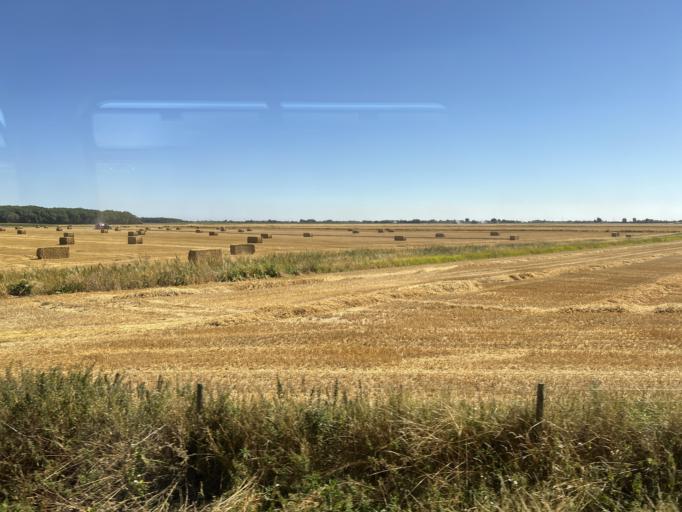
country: GB
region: England
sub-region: Lincolnshire
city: Spilsby
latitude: 53.1052
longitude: 0.1170
